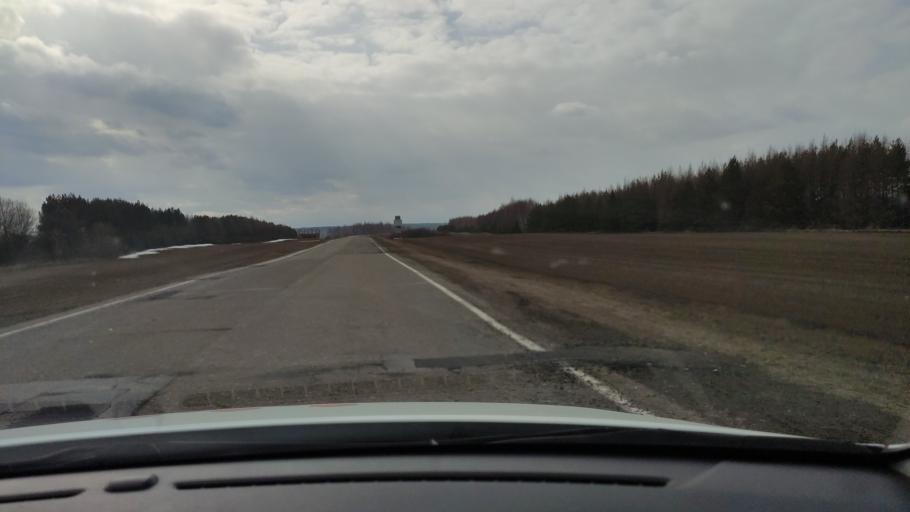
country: RU
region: Tatarstan
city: Vysokaya Gora
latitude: 56.1994
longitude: 49.2330
